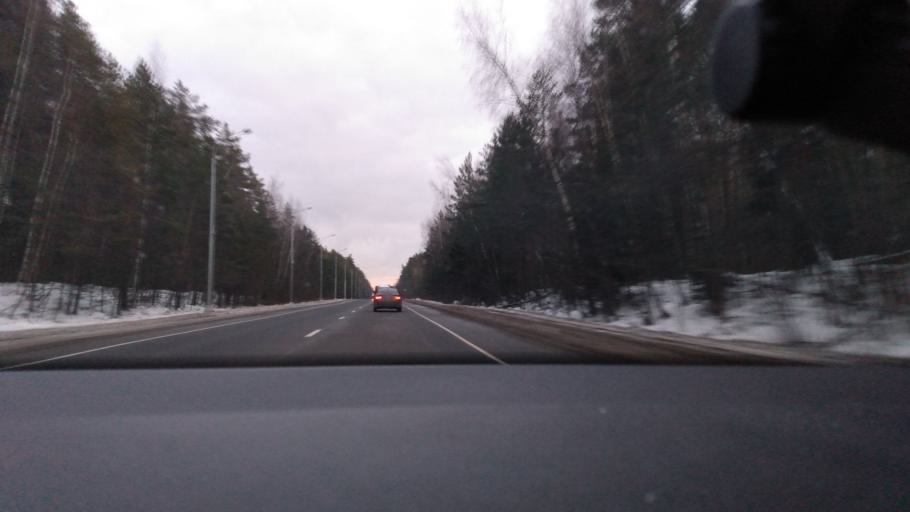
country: RU
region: Moskovskaya
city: Il'inskiy Pogost
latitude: 55.4690
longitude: 38.9654
